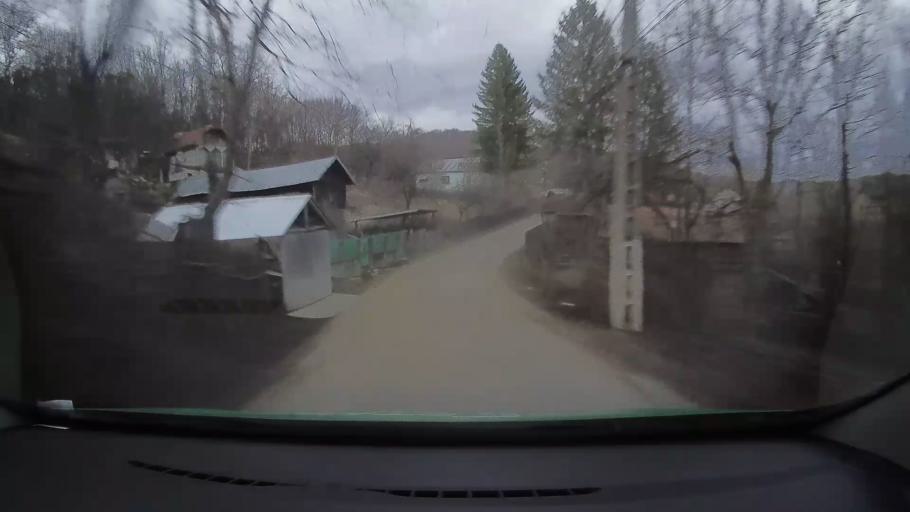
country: RO
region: Prahova
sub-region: Comuna Adunati
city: Adunati
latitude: 45.1143
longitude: 25.5869
